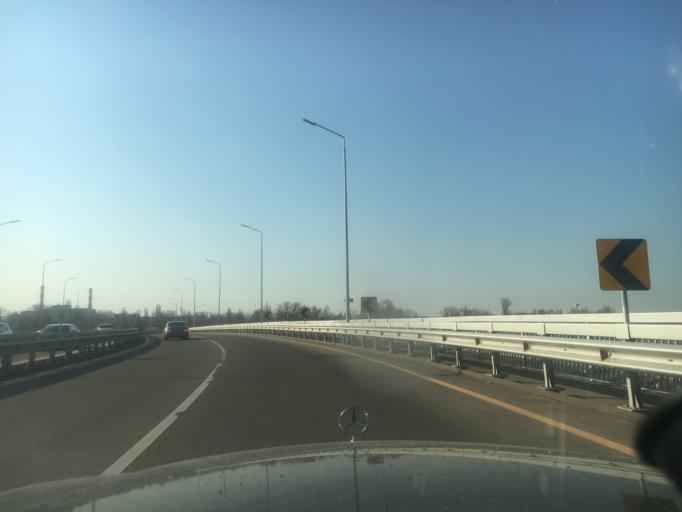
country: KZ
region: Almaty Qalasy
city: Almaty
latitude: 43.2759
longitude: 76.9449
